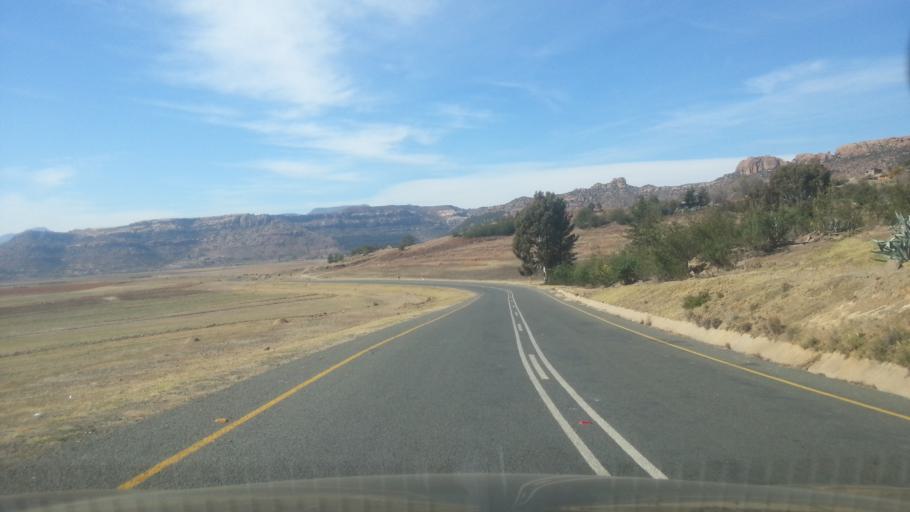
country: LS
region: Maseru
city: Nako
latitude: -29.5055
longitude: 27.6030
